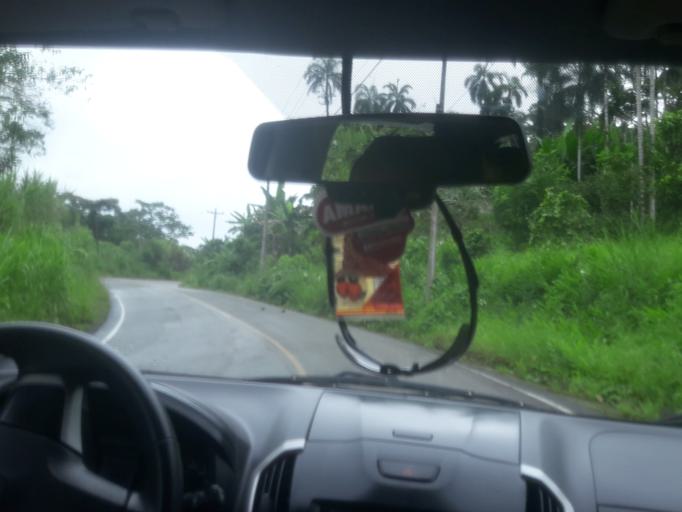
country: EC
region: Napo
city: Tena
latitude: -1.0385
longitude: -77.7122
